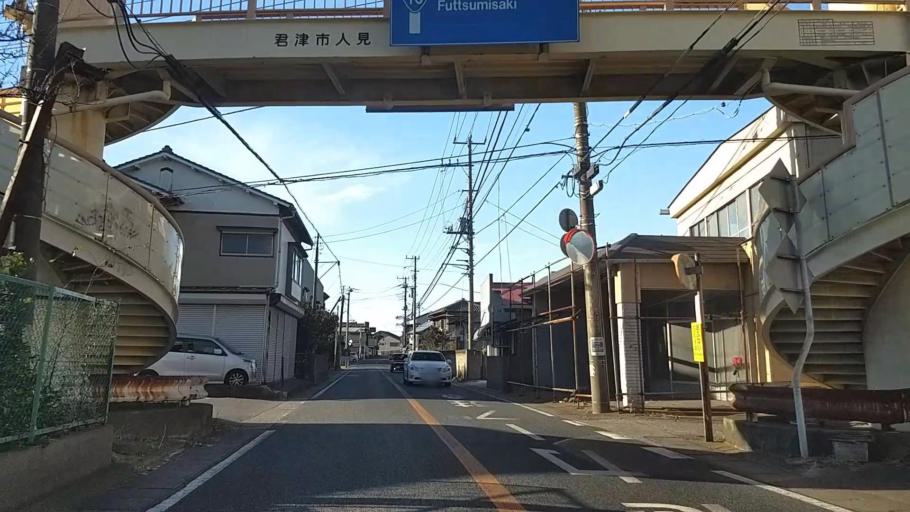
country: JP
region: Chiba
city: Kimitsu
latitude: 35.3407
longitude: 139.8664
